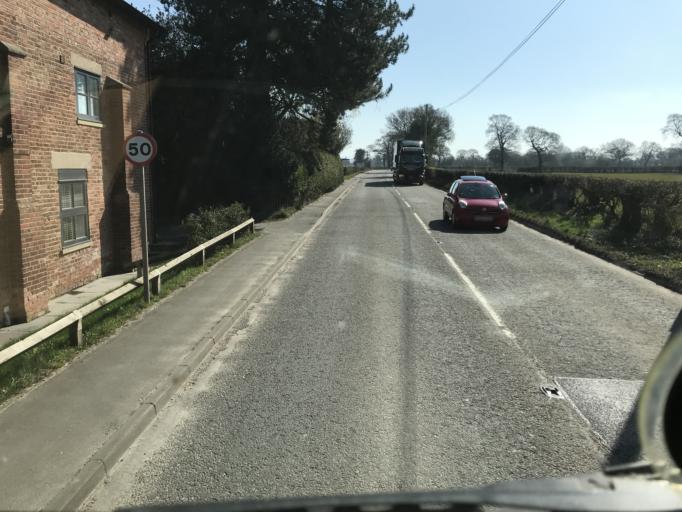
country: GB
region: England
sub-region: Cheshire East
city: Mobberley
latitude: 53.2770
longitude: -2.3003
